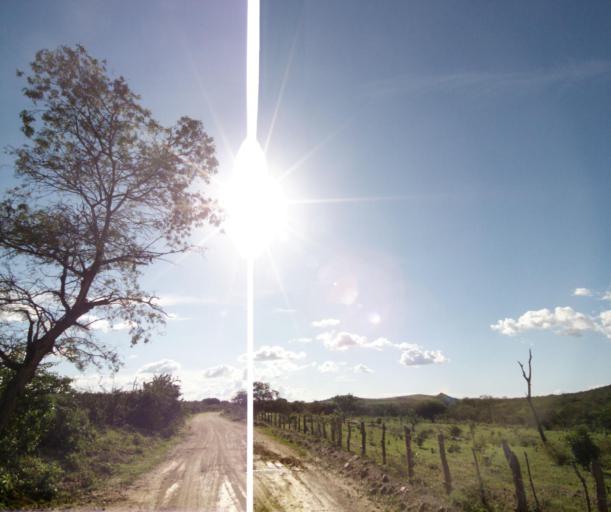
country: BR
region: Bahia
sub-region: Tanhacu
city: Tanhacu
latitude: -14.1873
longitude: -40.9534
